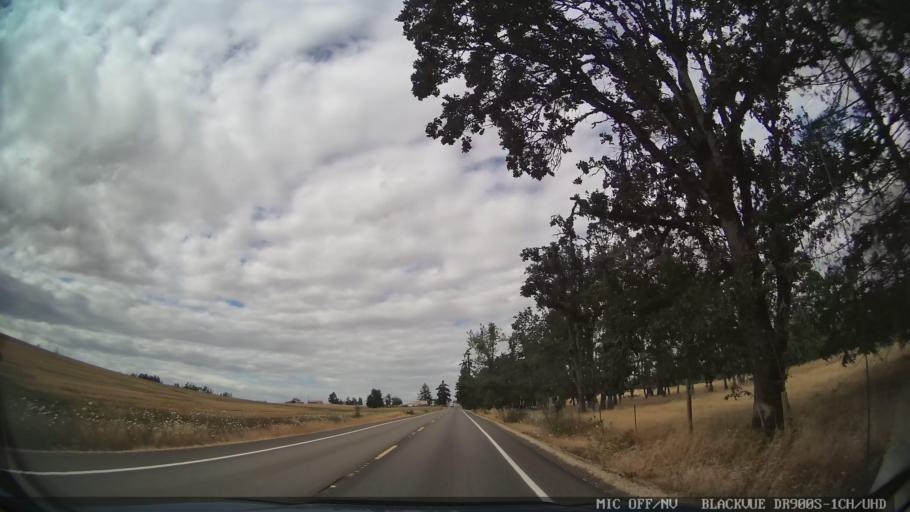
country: US
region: Oregon
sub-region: Marion County
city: Sublimity
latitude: 44.8555
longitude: -122.7931
